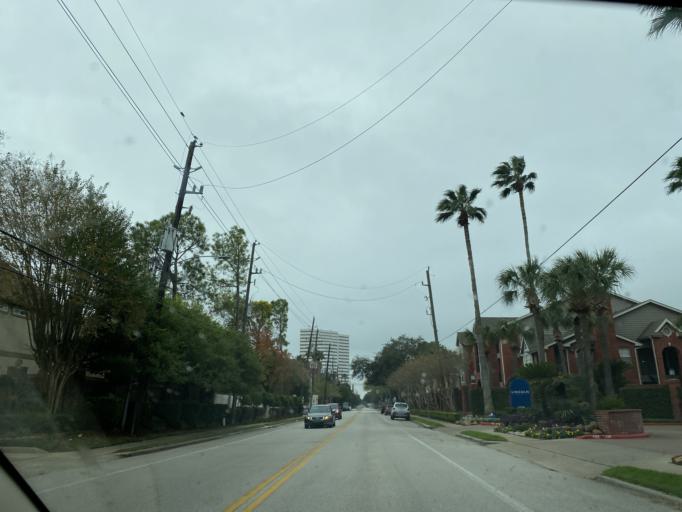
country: US
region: Texas
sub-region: Harris County
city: Hunters Creek Village
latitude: 29.7446
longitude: -95.4795
